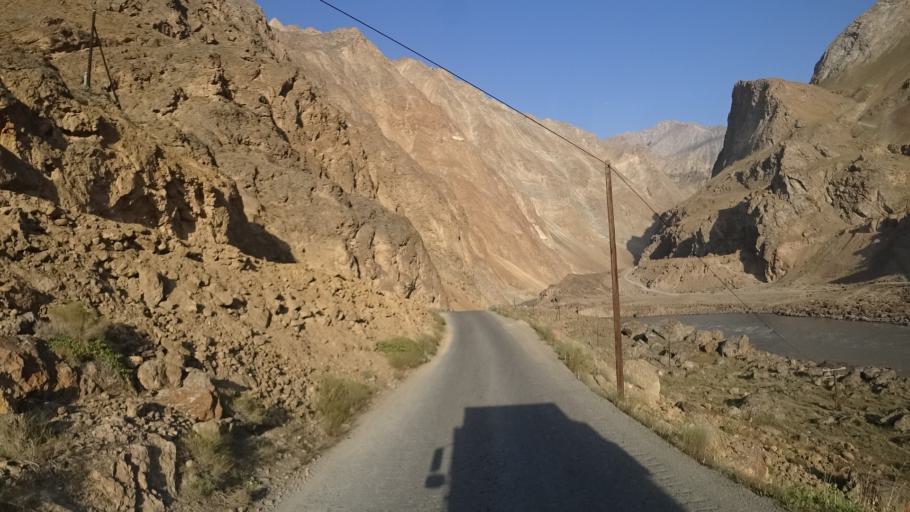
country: TJ
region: Gorno-Badakhshan
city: Vanj
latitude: 38.2725
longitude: 71.3492
